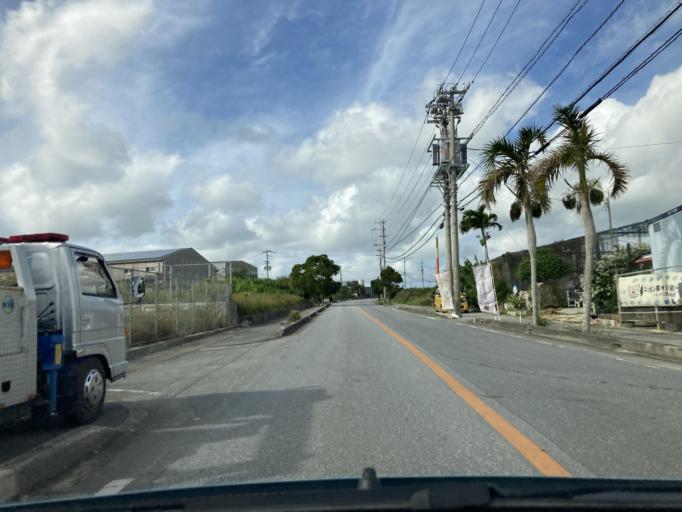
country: JP
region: Okinawa
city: Itoman
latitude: 26.1101
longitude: 127.7194
